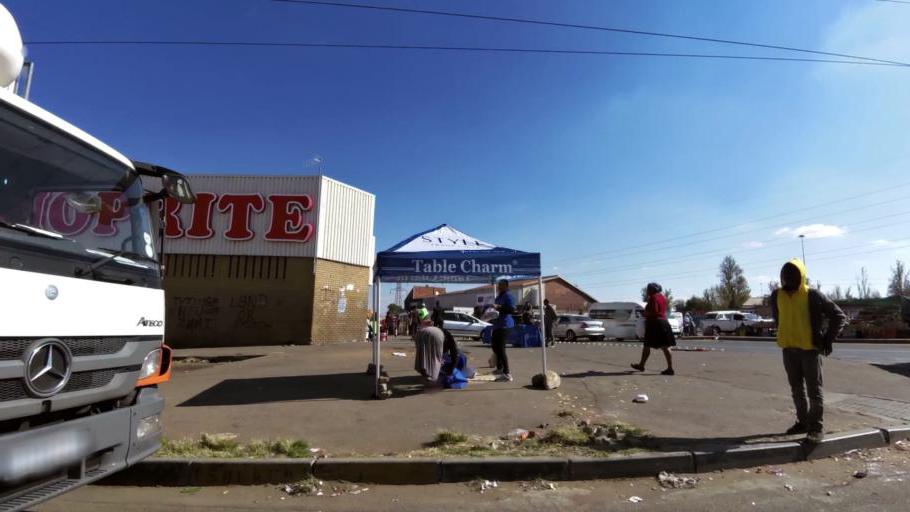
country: ZA
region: Gauteng
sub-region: City of Johannesburg Metropolitan Municipality
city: Soweto
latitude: -26.2377
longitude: 27.9010
